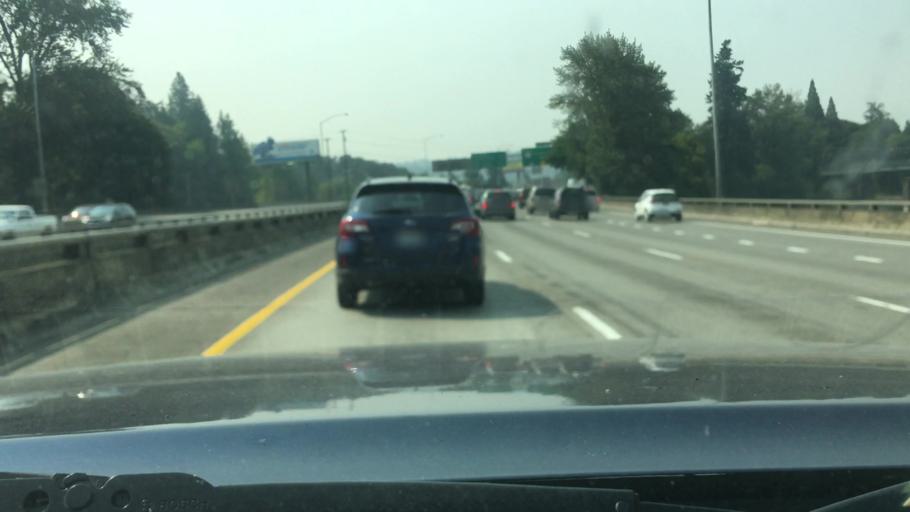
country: US
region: Oregon
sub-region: Clackamas County
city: Gladstone
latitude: 45.3806
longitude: -122.5808
